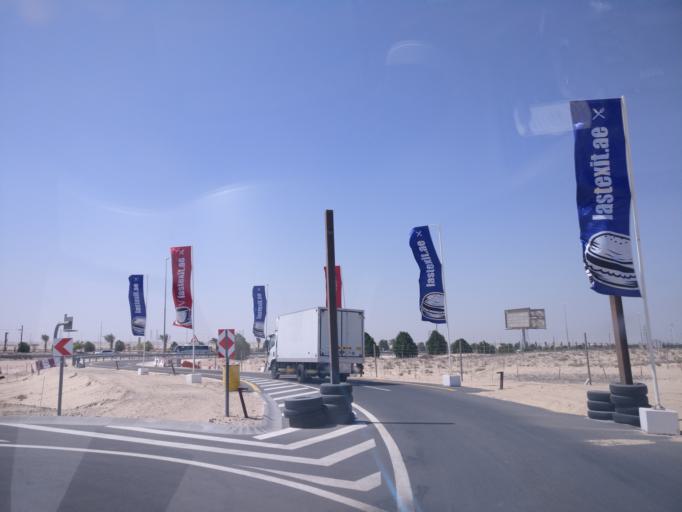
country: AE
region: Dubai
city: Dubai
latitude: 24.9127
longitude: 54.9594
